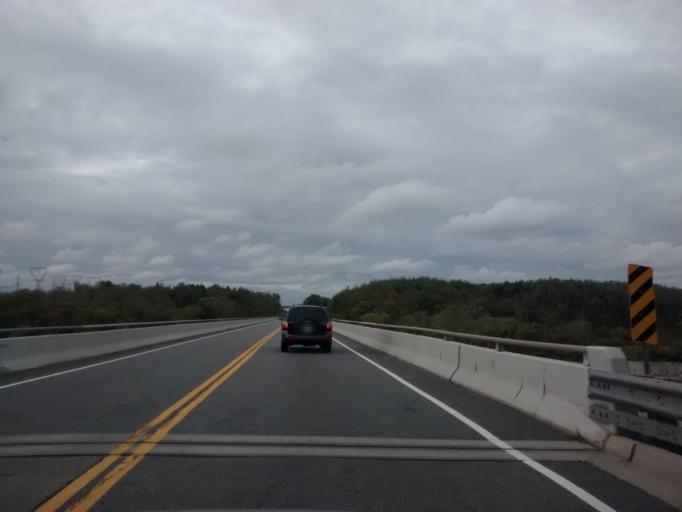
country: CA
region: Ontario
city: Ancaster
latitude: 43.0787
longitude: -79.9709
